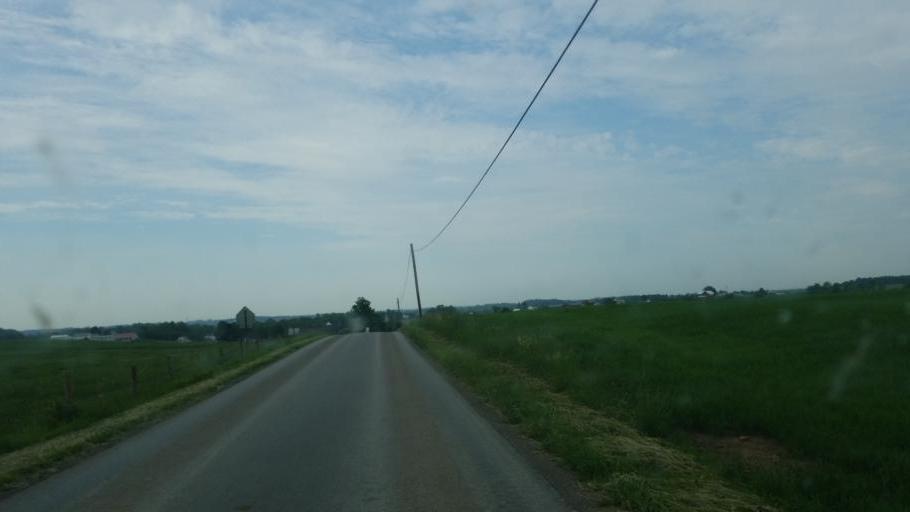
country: US
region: Ohio
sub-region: Wayne County
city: Apple Creek
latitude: 40.6600
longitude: -81.7651
